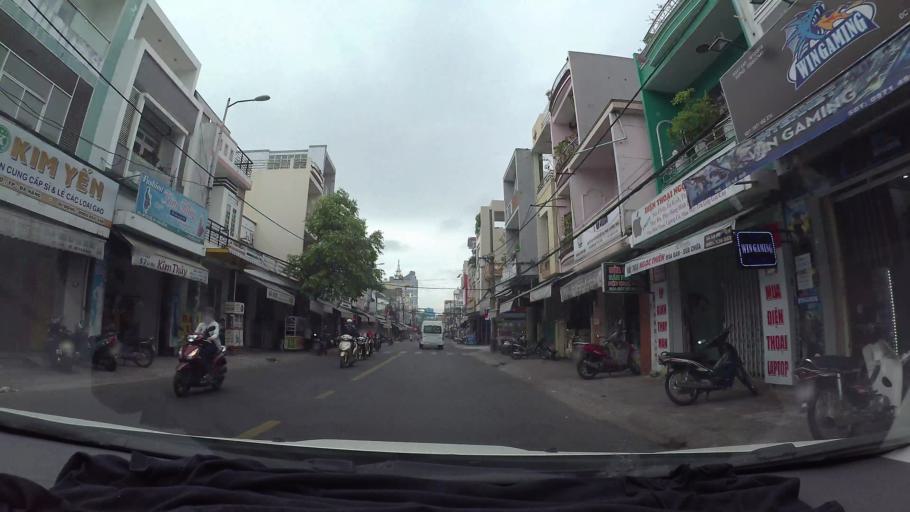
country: VN
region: Da Nang
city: Thanh Khe
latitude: 16.0692
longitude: 108.2016
